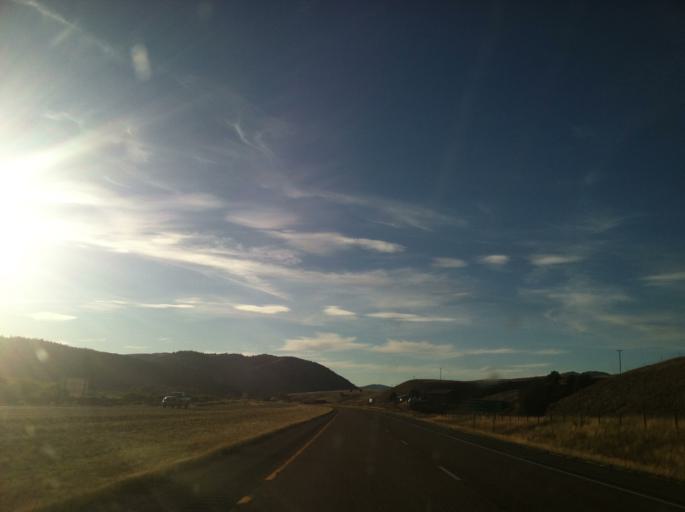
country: US
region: Montana
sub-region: Granite County
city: Philipsburg
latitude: 46.6766
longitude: -113.1709
